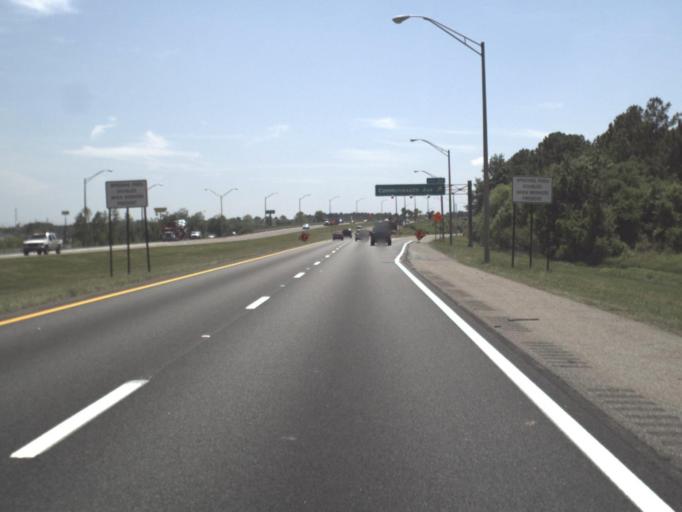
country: US
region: Florida
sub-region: Duval County
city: Jacksonville
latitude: 30.3410
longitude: -81.7609
